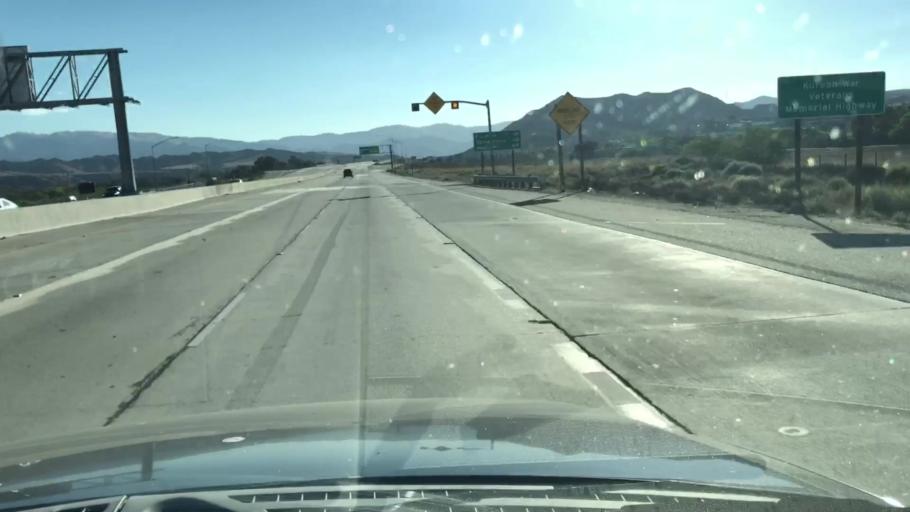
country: US
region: California
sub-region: Los Angeles County
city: Valencia
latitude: 34.4394
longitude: -118.6115
